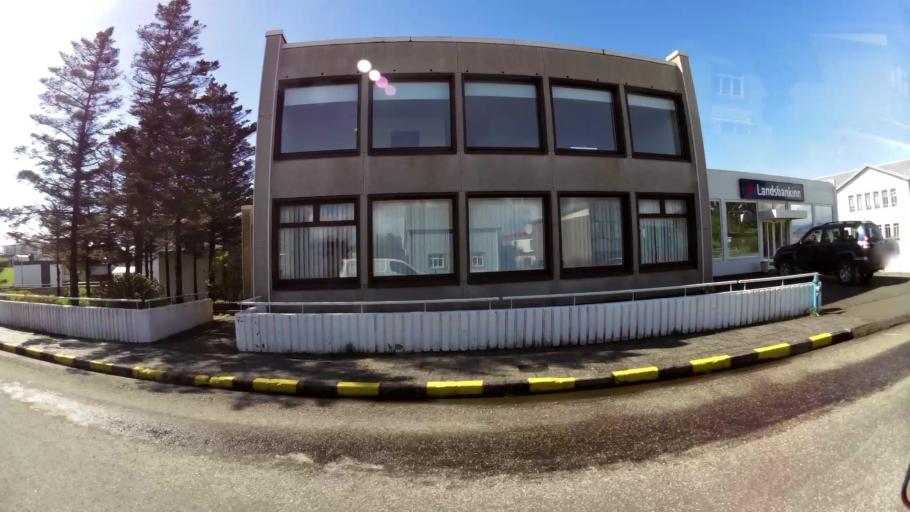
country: IS
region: East
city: Hoefn
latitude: 64.2510
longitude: -15.2088
